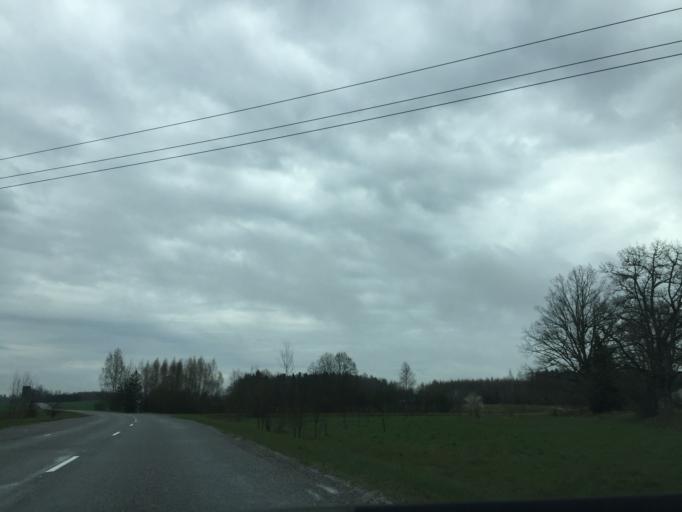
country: LV
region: Malpils
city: Malpils
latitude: 57.0105
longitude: 24.8974
